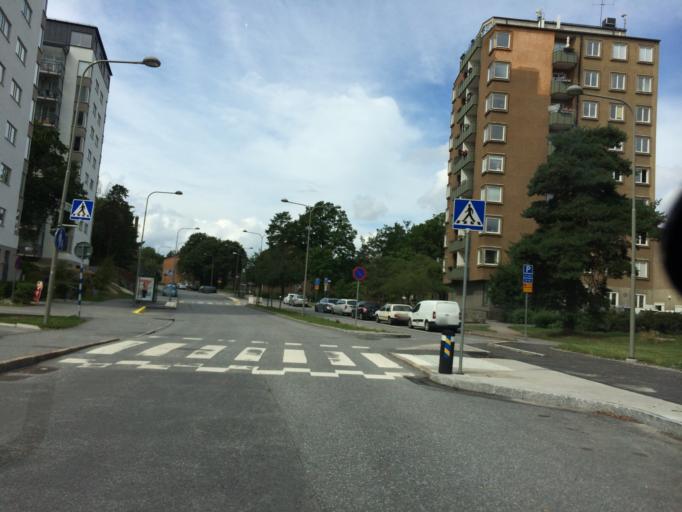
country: SE
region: Stockholm
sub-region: Stockholms Kommun
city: Arsta
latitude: 59.2862
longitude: 18.0102
